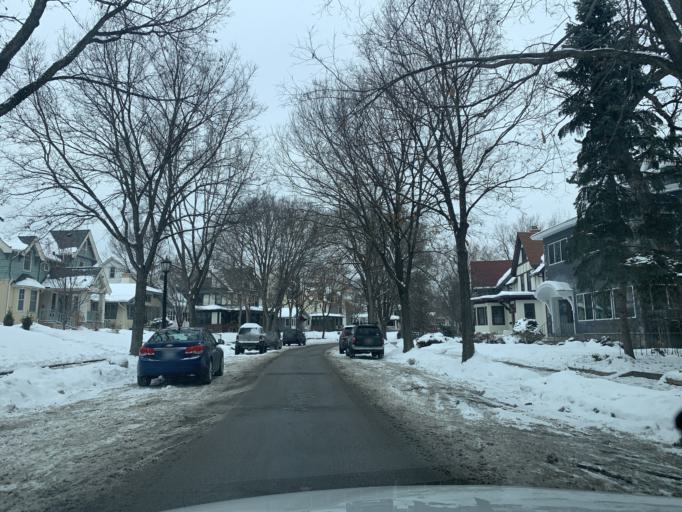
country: US
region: Minnesota
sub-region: Hennepin County
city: Saint Louis Park
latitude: 44.9512
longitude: -93.3021
